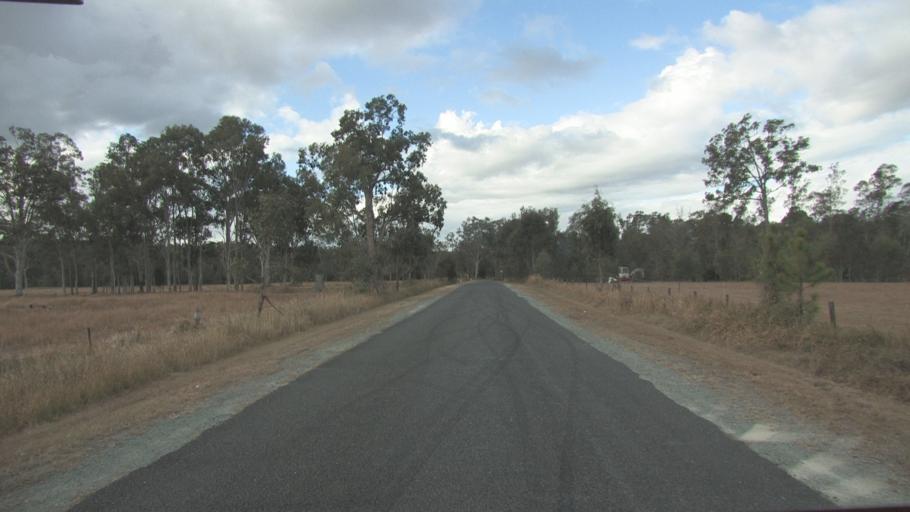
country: AU
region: Queensland
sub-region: Logan
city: Cedar Vale
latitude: -27.8865
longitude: 153.0745
